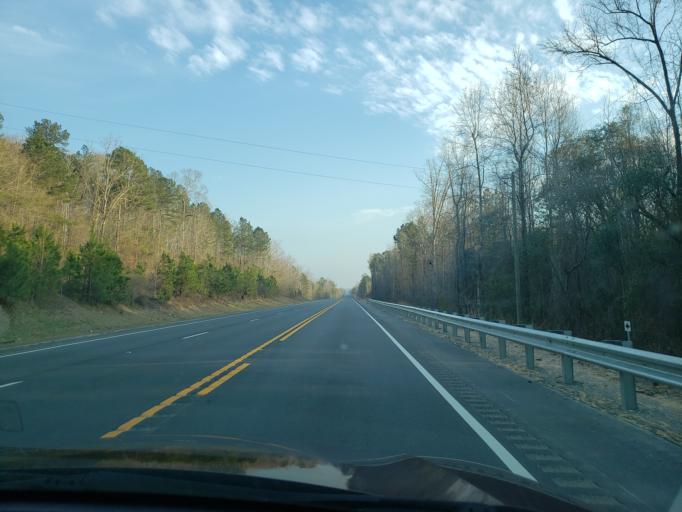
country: US
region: Alabama
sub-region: Hale County
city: Moundville
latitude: 32.8541
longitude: -87.6129
